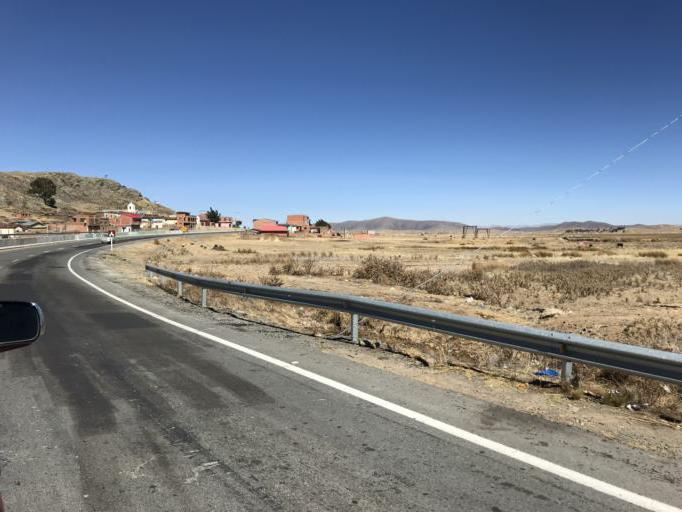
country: BO
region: La Paz
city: Batallas
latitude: -16.2468
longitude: -68.5699
